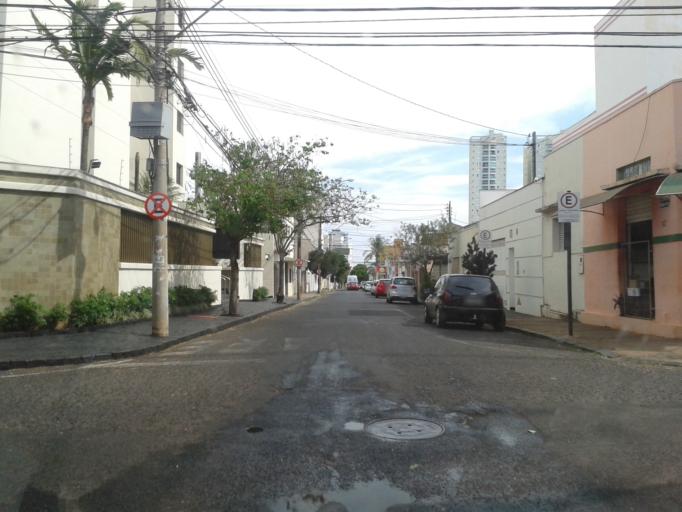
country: BR
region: Minas Gerais
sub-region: Uberlandia
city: Uberlandia
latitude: -18.9174
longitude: -48.2718
